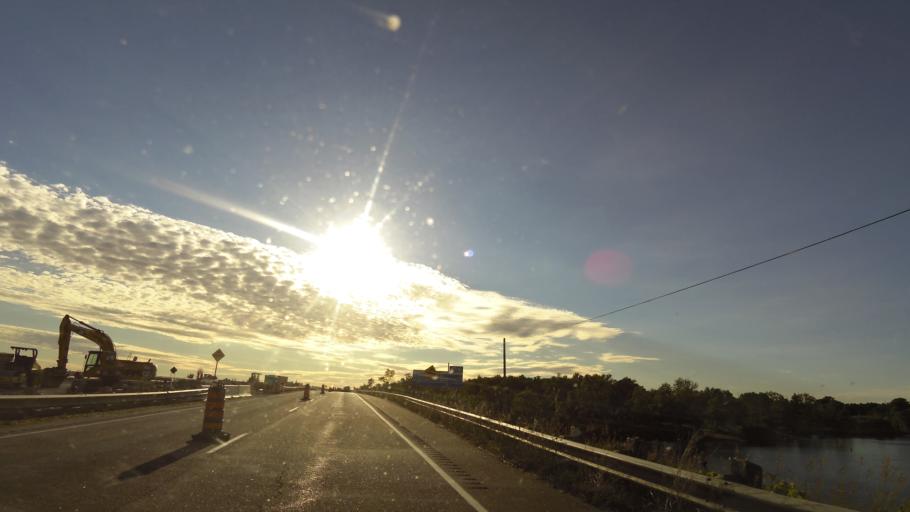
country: CA
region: Ontario
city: Midland
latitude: 44.7995
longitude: -79.7204
